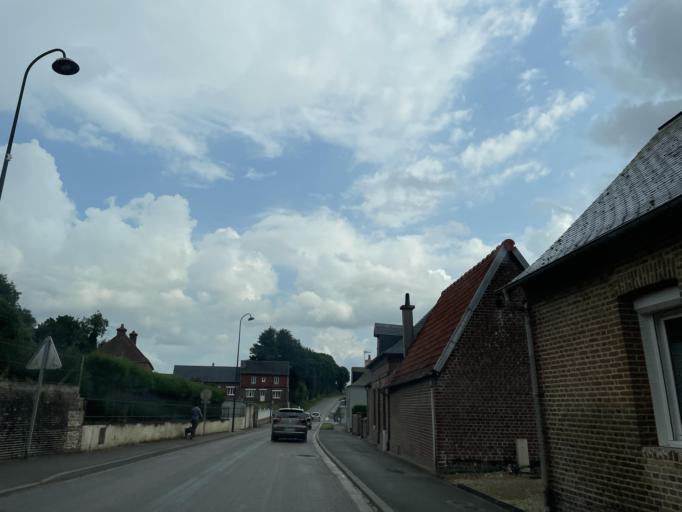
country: FR
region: Haute-Normandie
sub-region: Departement de la Seine-Maritime
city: Envermeu
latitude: 49.8898
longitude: 1.2789
